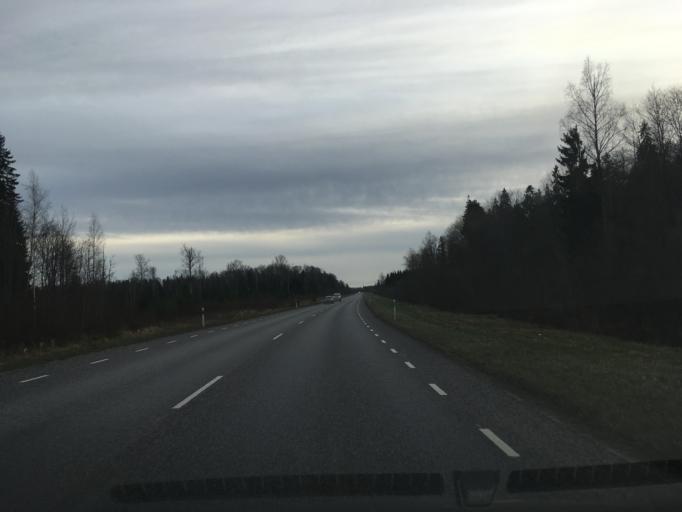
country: EE
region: Ida-Virumaa
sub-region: Johvi vald
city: Johvi
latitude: 59.3521
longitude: 27.4674
